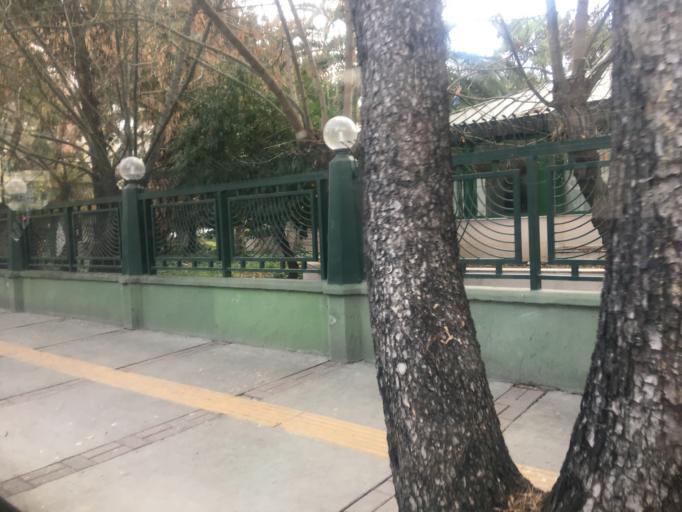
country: TR
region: Izmir
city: Izmir
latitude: 38.4312
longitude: 27.1428
